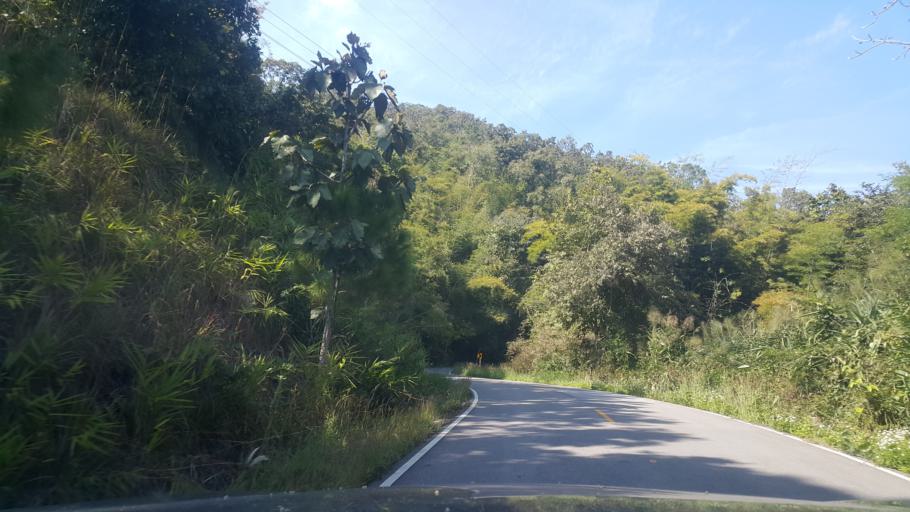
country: TH
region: Chiang Mai
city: Samoeng
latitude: 18.9012
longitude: 98.6767
